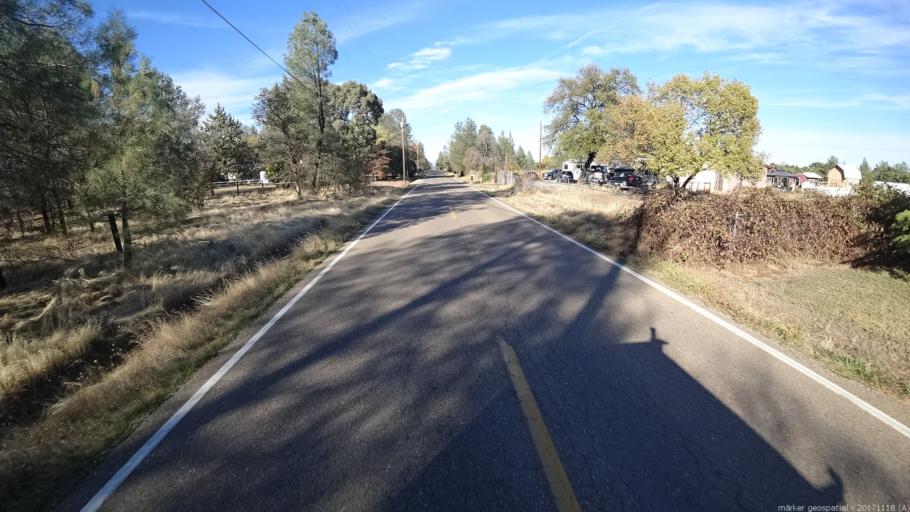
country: US
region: California
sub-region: Shasta County
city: Redding
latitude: 40.4539
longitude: -122.4545
